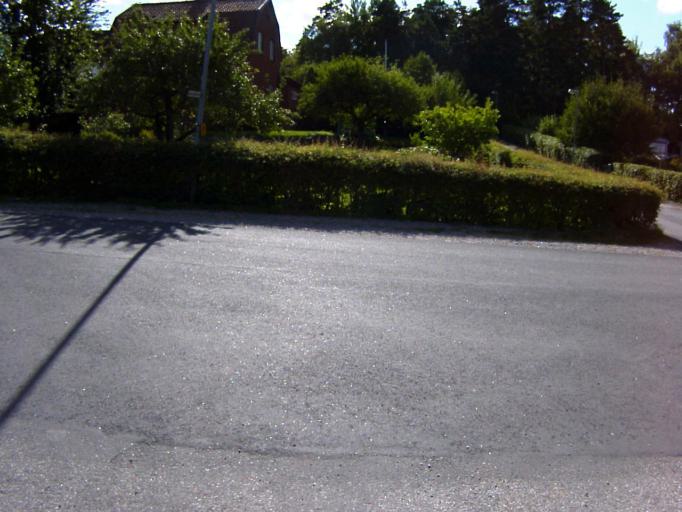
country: SE
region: Soedermanland
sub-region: Eskilstuna Kommun
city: Eskilstuna
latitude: 59.3720
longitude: 16.4899
